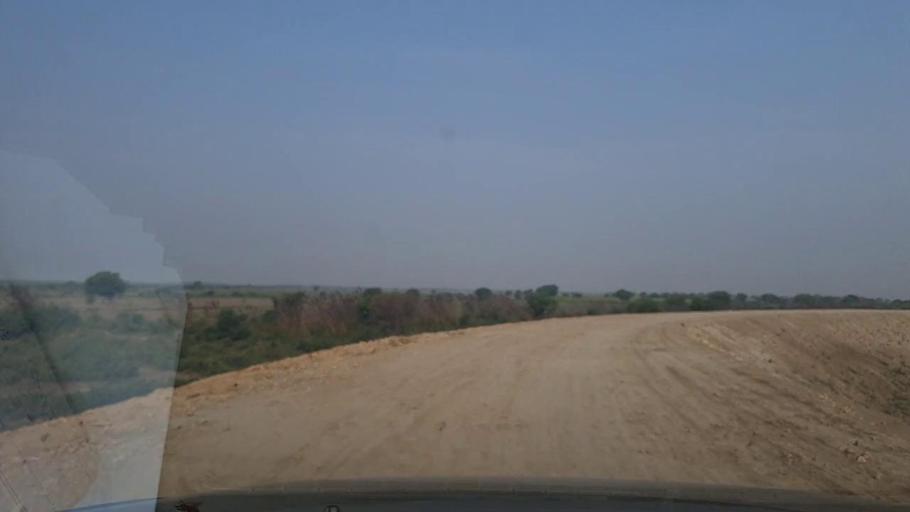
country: PK
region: Sindh
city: Bulri
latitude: 24.9678
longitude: 68.2900
